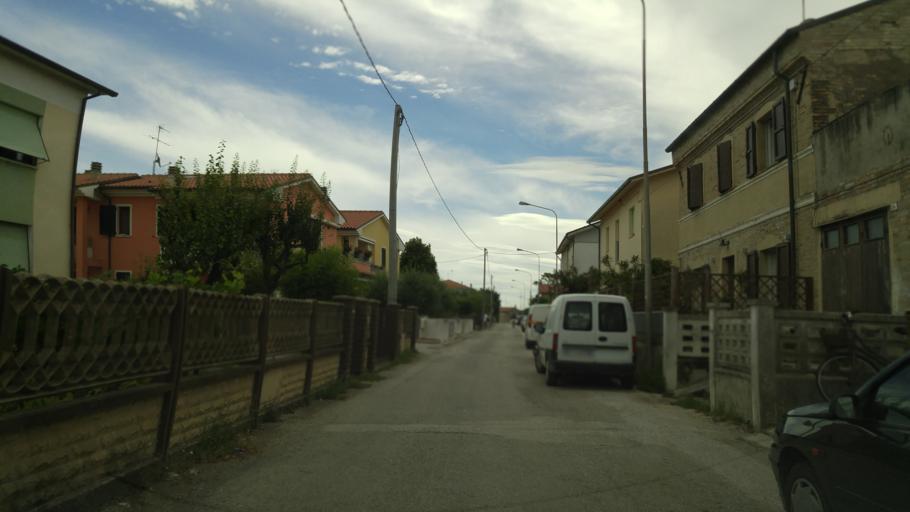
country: IT
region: The Marches
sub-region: Provincia di Pesaro e Urbino
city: Centinarola
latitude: 43.8594
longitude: 12.9928
